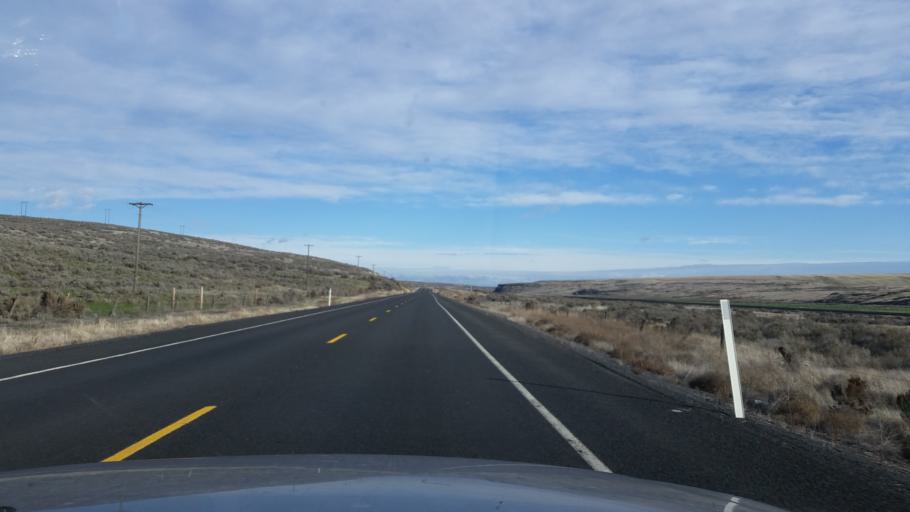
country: US
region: Washington
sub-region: Adams County
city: Ritzville
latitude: 47.3498
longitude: -118.5477
